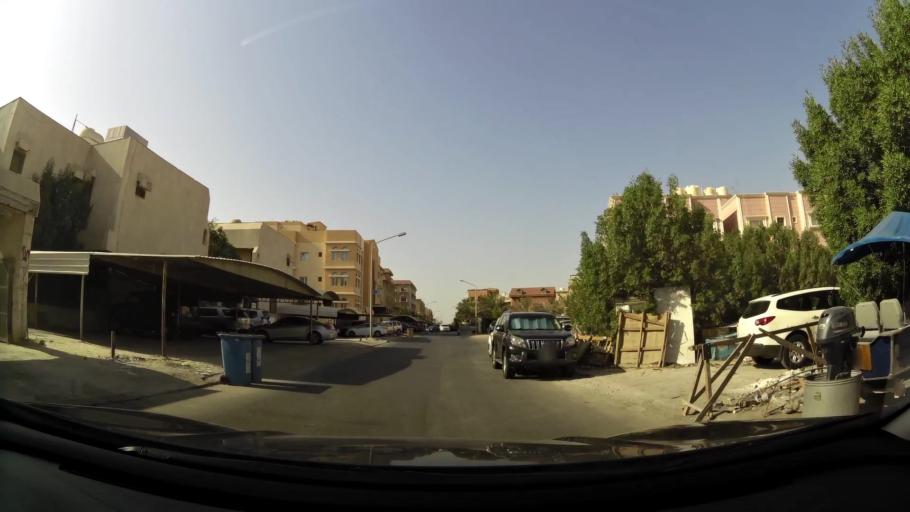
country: KW
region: Muhafazat Hawalli
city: Salwa
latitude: 29.2968
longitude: 48.0685
